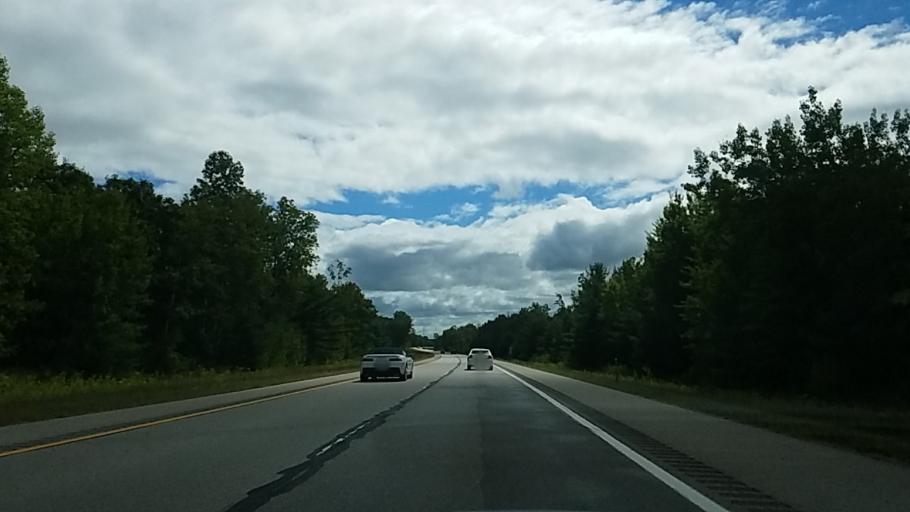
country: US
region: Michigan
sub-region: Ogemaw County
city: Skidway Lake
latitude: 44.0630
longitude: -84.0860
